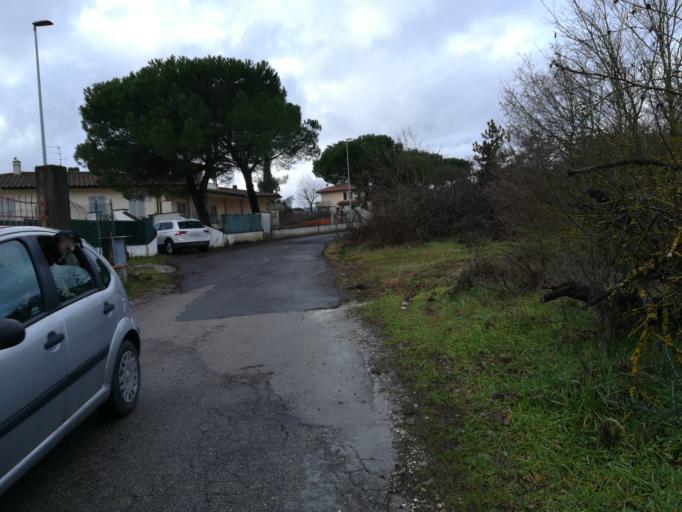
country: IT
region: Tuscany
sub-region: Provincia di Prato
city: Comeana
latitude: 43.7999
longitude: 11.0552
